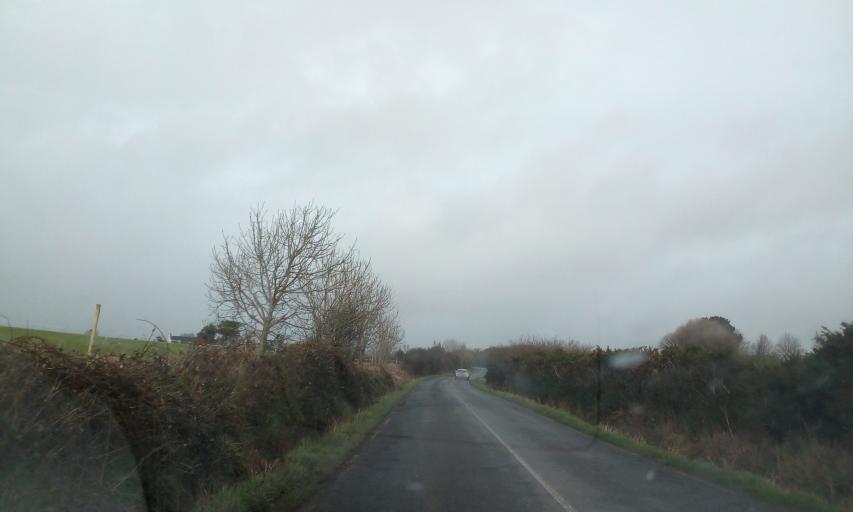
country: IE
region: Leinster
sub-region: Loch Garman
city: New Ross
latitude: 52.2566
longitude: -6.7554
